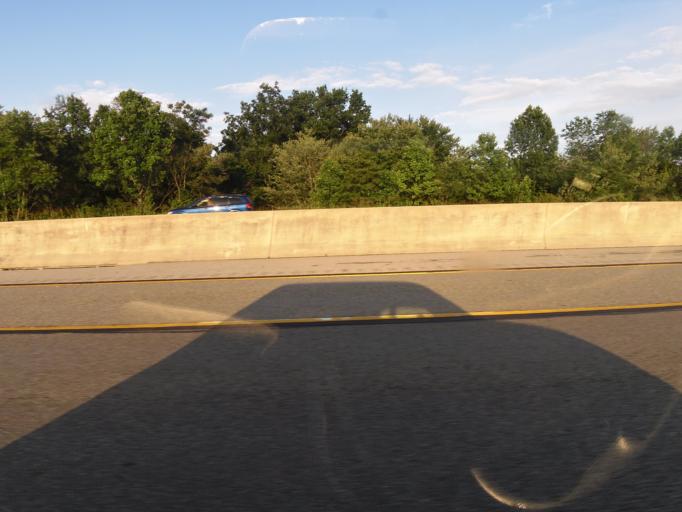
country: US
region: Kentucky
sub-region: Madison County
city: Berea
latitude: 37.4889
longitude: -84.3304
